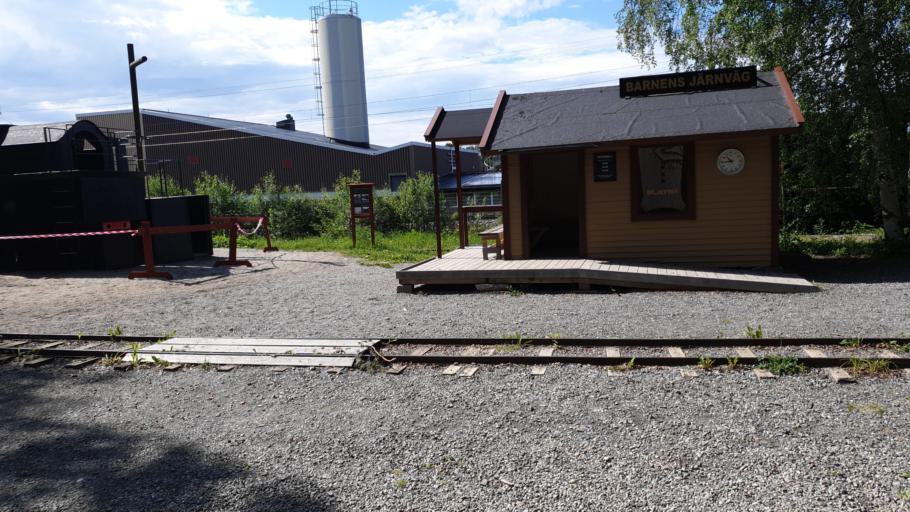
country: SE
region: Jaemtland
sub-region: OEstersunds Kommun
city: Ostersund
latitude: 63.1927
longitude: 14.6370
